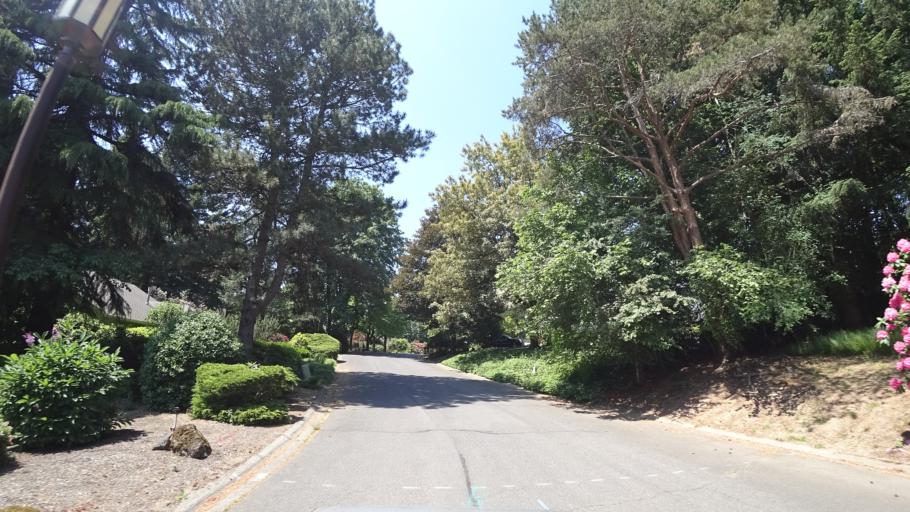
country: US
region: Oregon
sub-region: Washington County
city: Metzger
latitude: 45.4296
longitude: -122.7200
